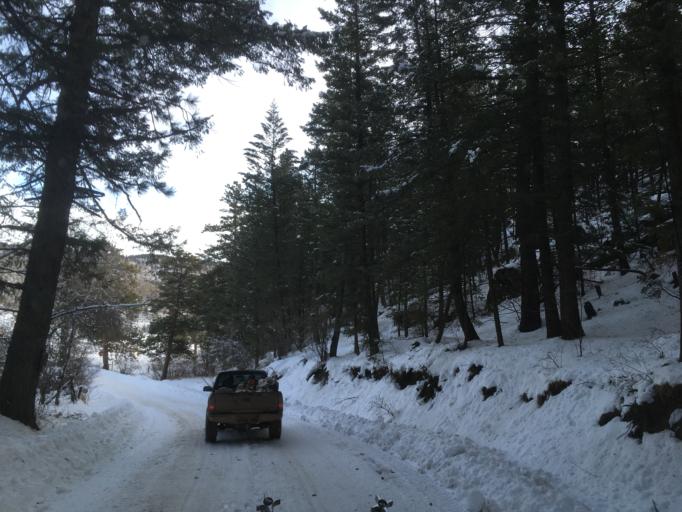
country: US
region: Wyoming
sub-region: Albany County
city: Laramie
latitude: 40.9184
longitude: -105.5071
